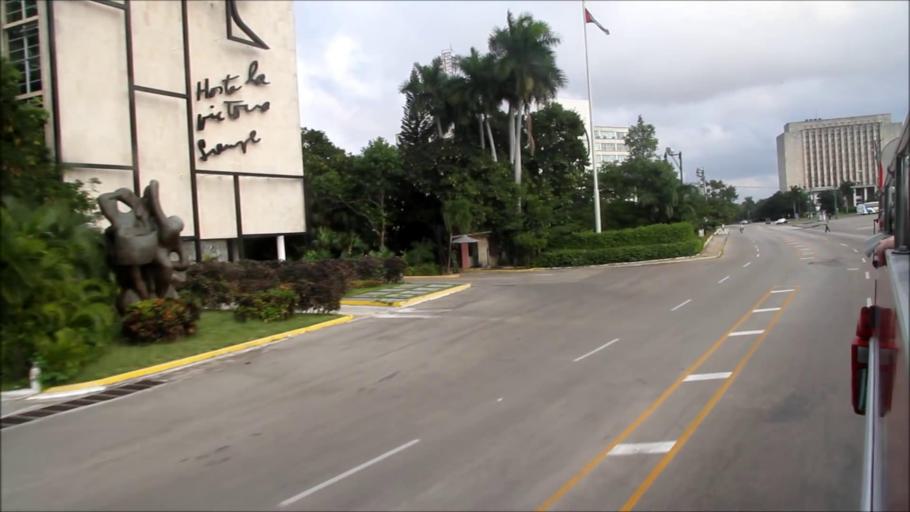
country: CU
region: La Habana
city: Havana
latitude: 23.1262
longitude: -82.3864
